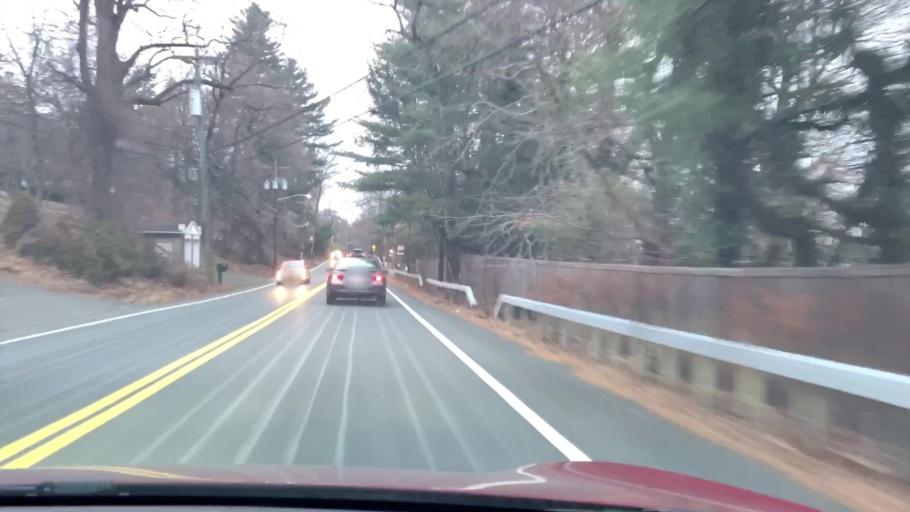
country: US
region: New York
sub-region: Rockland County
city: South Nyack
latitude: 41.0627
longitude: -73.9232
